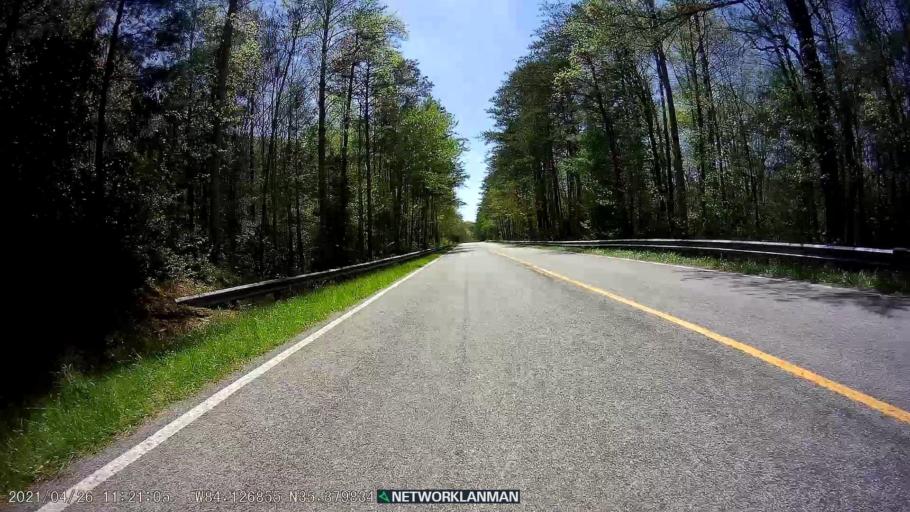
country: US
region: Tennessee
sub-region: Monroe County
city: Vonore
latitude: 35.3801
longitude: -84.1266
